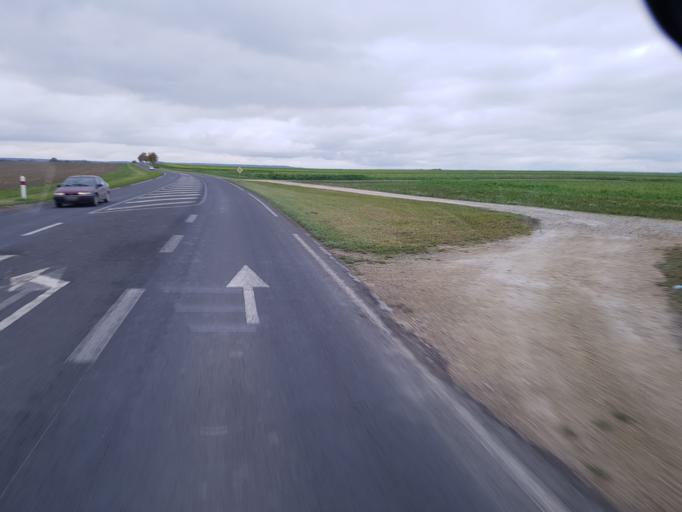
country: FR
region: Champagne-Ardenne
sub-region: Departement de la Marne
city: Saint-Just-Sauvage
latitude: 48.6230
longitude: 3.7890
